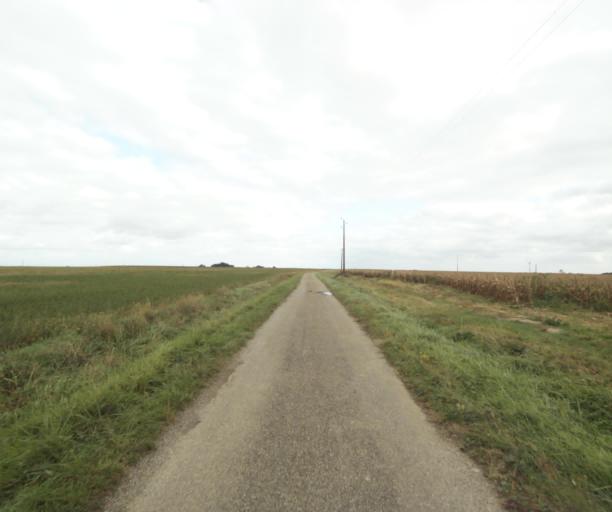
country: FR
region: Midi-Pyrenees
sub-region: Departement du Tarn-et-Garonne
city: Beaumont-de-Lomagne
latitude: 43.8876
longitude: 1.0887
